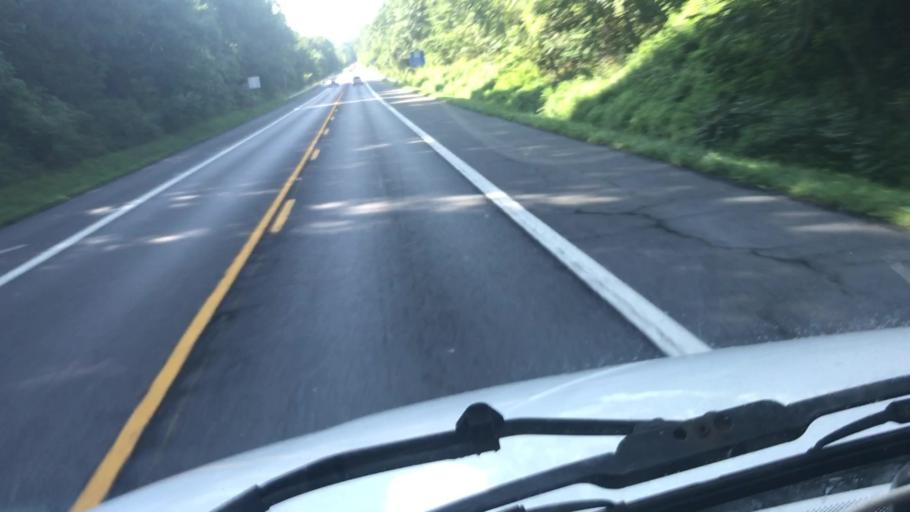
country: US
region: Maryland
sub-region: Howard County
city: Highland
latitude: 39.2454
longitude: -76.9777
